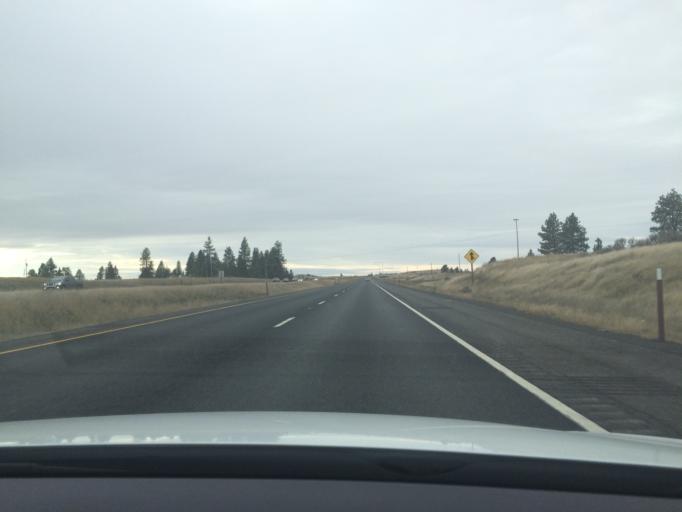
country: US
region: Washington
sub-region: Spokane County
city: Medical Lake
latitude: 47.3950
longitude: -117.8428
